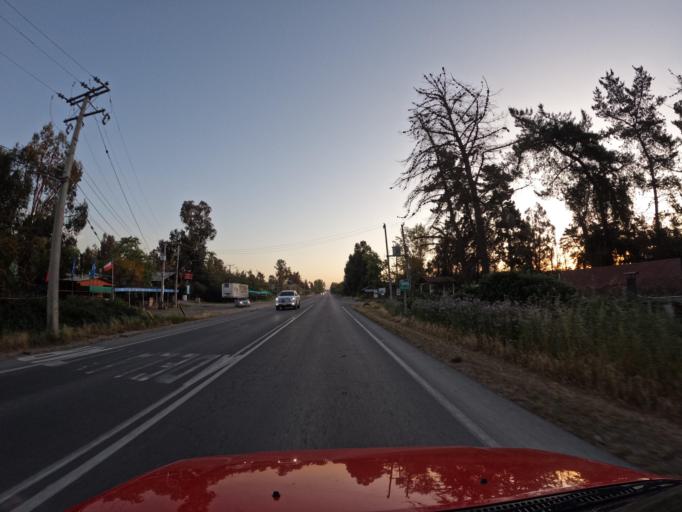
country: CL
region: O'Higgins
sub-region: Provincia de Cachapoal
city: San Vicente
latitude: -34.1511
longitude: -71.3845
